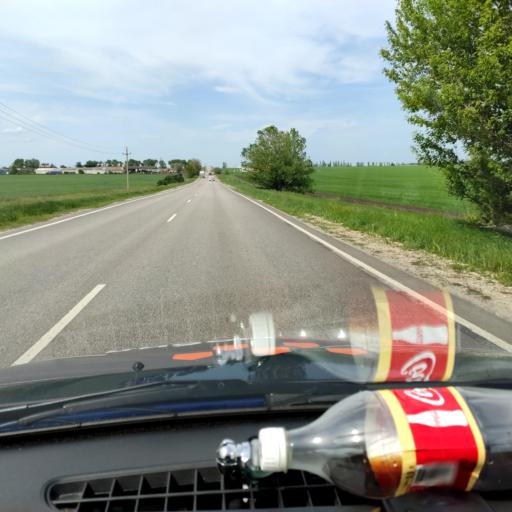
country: RU
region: Voronezj
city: Novaya Usman'
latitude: 51.5742
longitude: 39.3753
